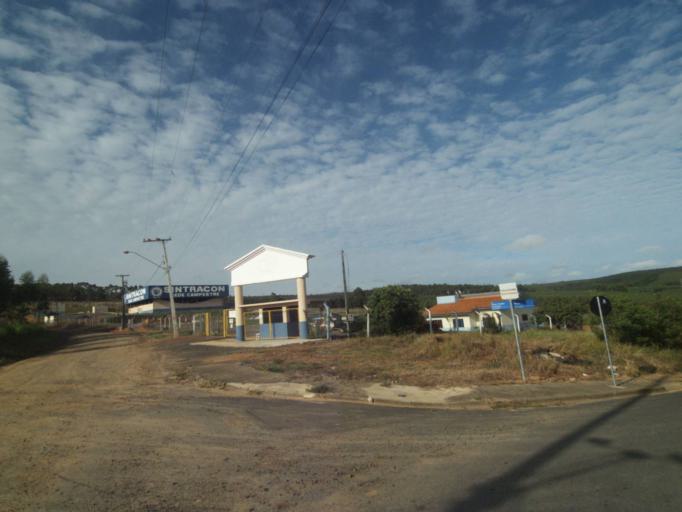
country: BR
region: Parana
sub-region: Telemaco Borba
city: Telemaco Borba
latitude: -24.3486
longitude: -50.6131
